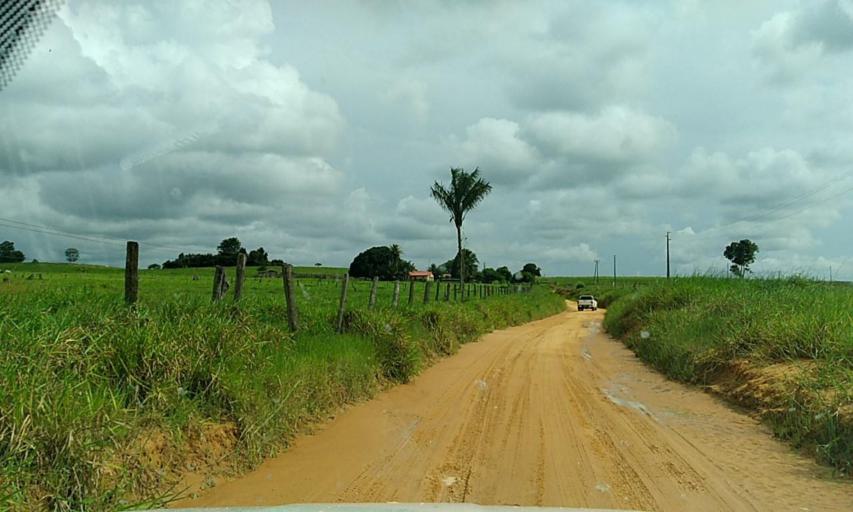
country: BR
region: Para
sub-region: Altamira
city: Altamira
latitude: -3.2507
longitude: -52.6941
